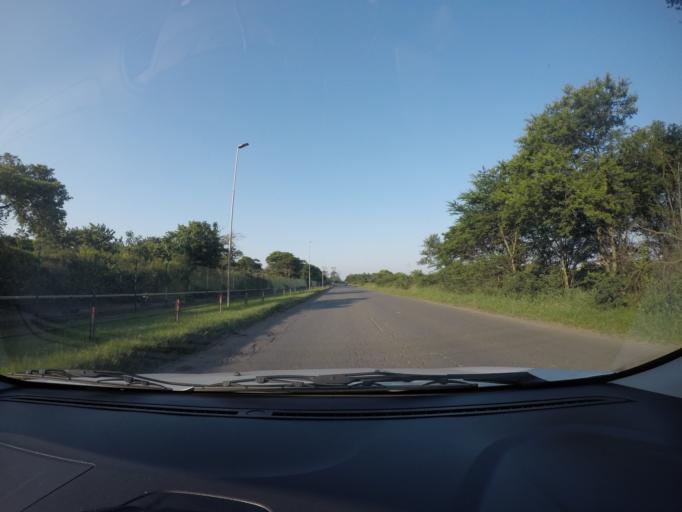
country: ZA
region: KwaZulu-Natal
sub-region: uThungulu District Municipality
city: Richards Bay
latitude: -28.7608
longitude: 32.0019
